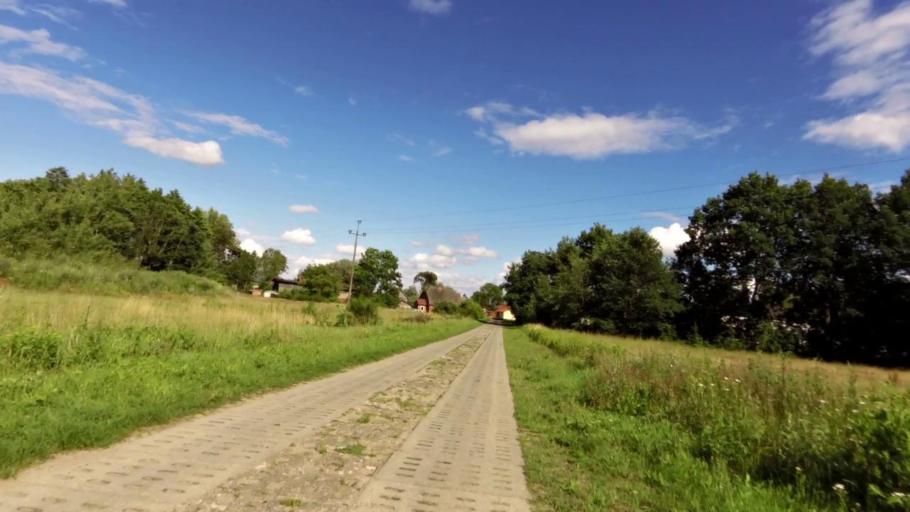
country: PL
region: West Pomeranian Voivodeship
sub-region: Powiat slawienski
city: Slawno
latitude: 54.4607
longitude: 16.7324
